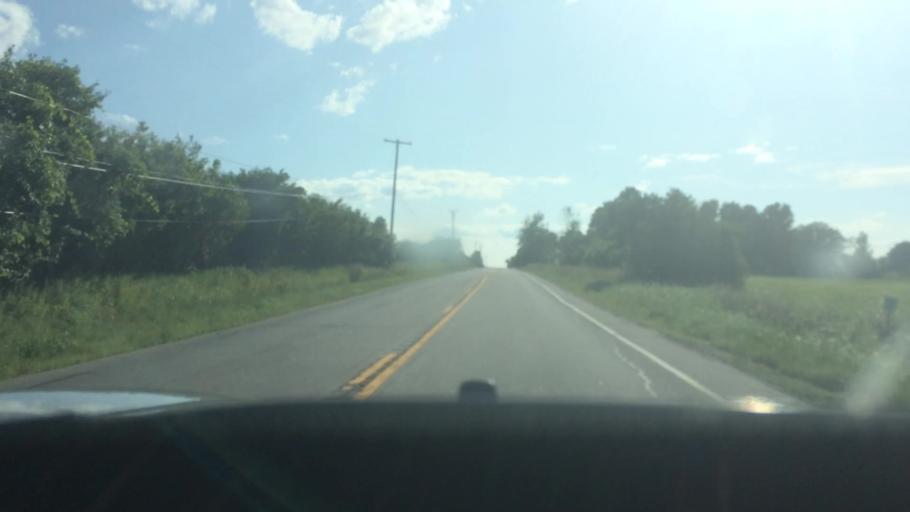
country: US
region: New York
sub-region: Franklin County
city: Malone
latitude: 44.7932
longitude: -74.4681
